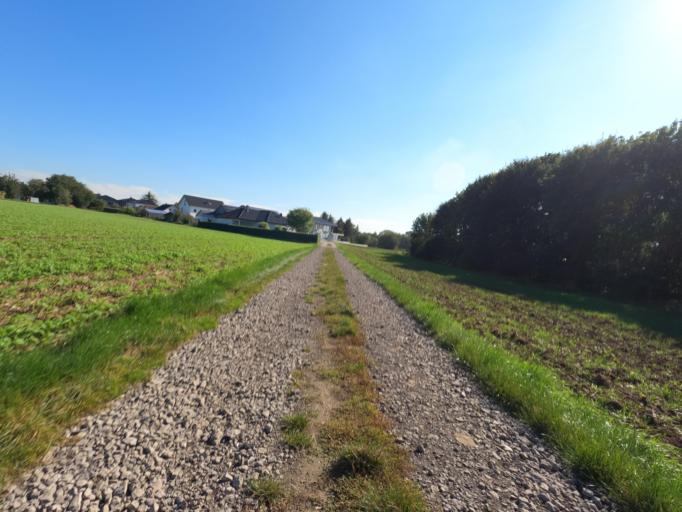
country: DE
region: North Rhine-Westphalia
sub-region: Regierungsbezirk Koln
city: Linnich
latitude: 50.9874
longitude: 6.3024
